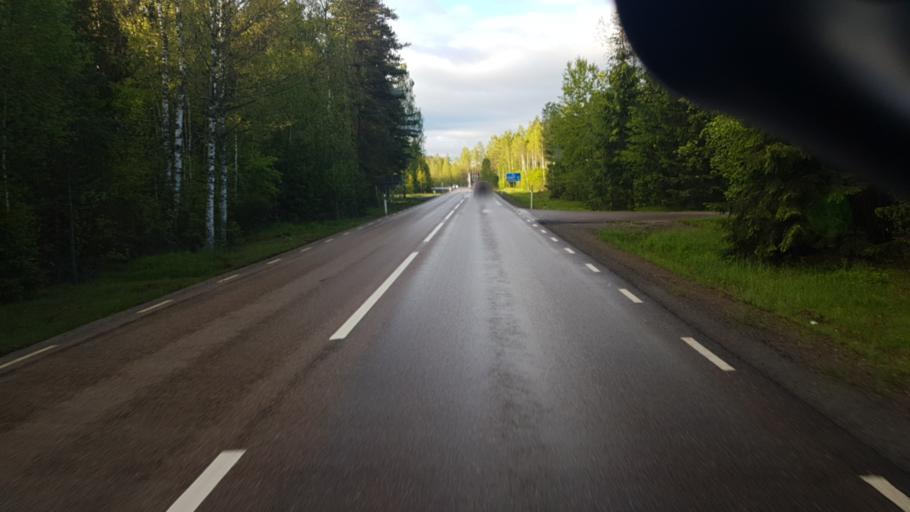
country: SE
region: Vaermland
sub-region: Eda Kommun
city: Charlottenberg
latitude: 59.8471
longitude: 12.3111
